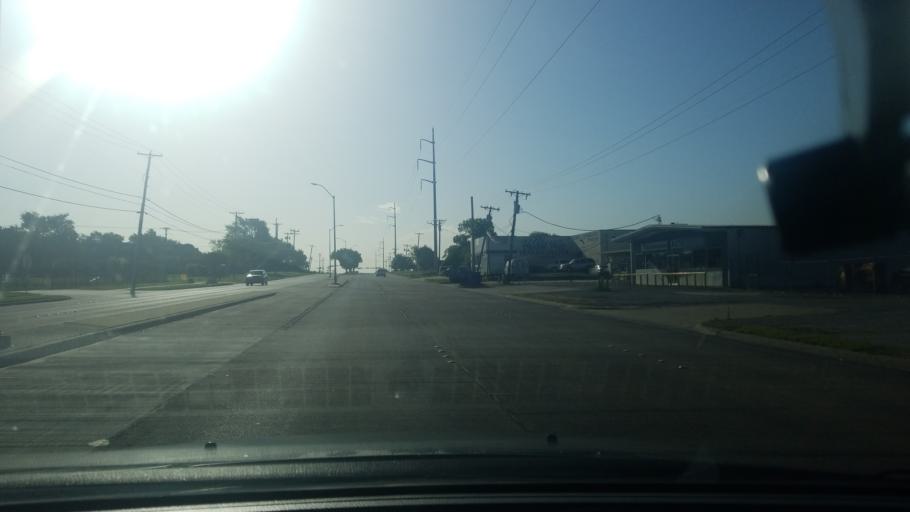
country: US
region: Texas
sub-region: Dallas County
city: Mesquite
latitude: 32.7923
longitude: -96.6725
